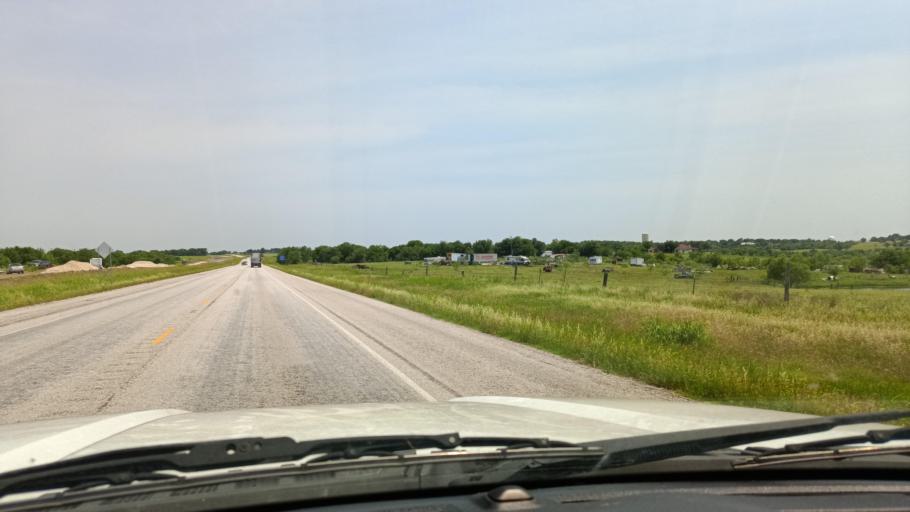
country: US
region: Texas
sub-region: Bell County
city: Rogers
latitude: 30.9641
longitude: -97.2632
